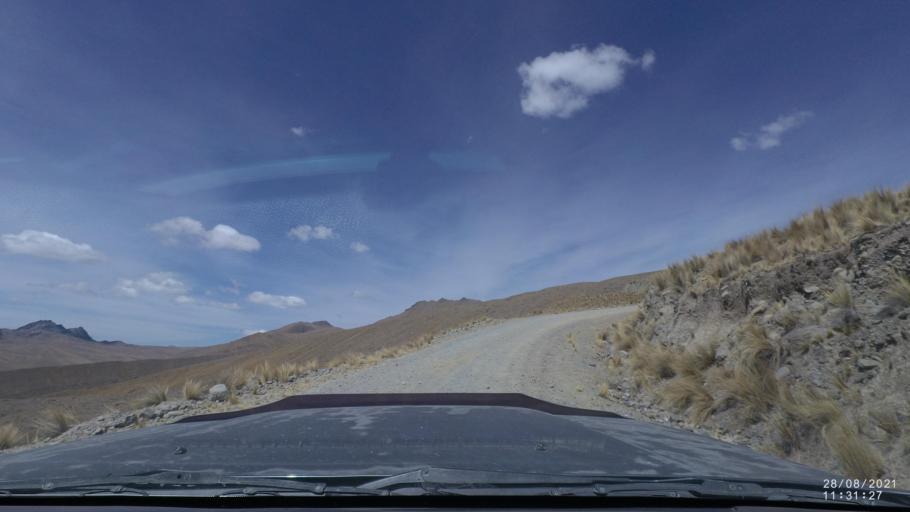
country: BO
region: Cochabamba
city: Sipe Sipe
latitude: -17.1828
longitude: -66.3653
